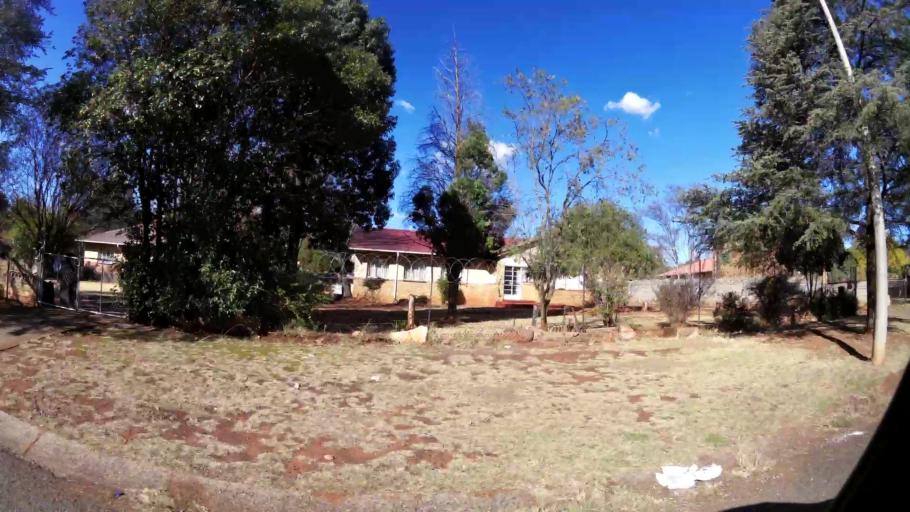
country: ZA
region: Gauteng
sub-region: West Rand District Municipality
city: Carletonville
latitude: -26.3725
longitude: 27.4043
